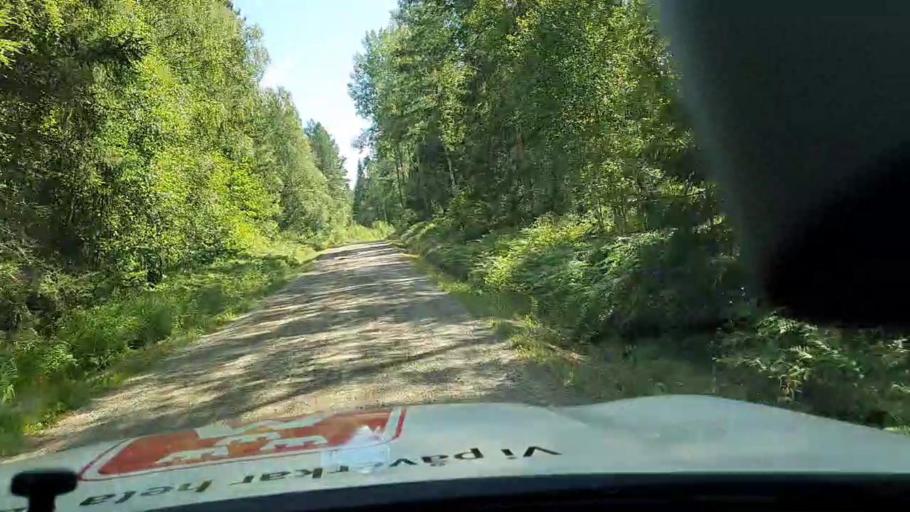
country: SE
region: Soedermanland
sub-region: Strangnas Kommun
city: Akers Styckebruk
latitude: 59.2087
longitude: 16.9166
